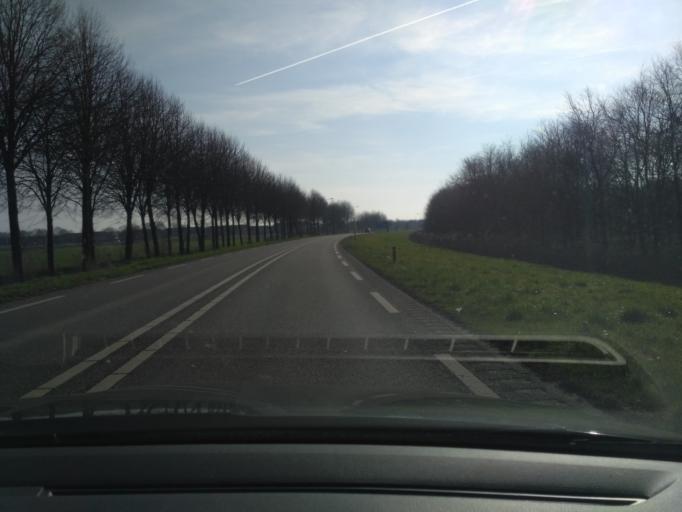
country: NL
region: Flevoland
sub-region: Gemeente Zeewolde
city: Zeewolde
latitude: 52.3460
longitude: 5.5051
